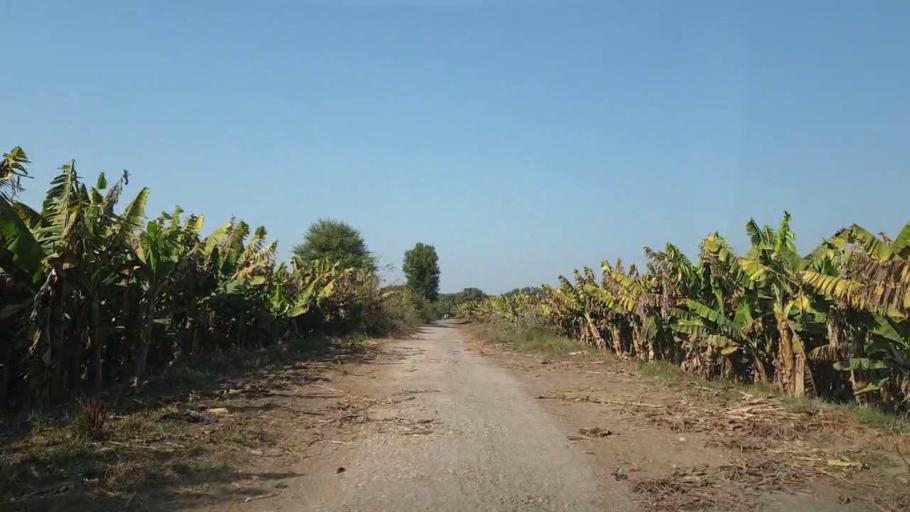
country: PK
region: Sindh
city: Tando Jam
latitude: 25.5035
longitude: 68.5368
